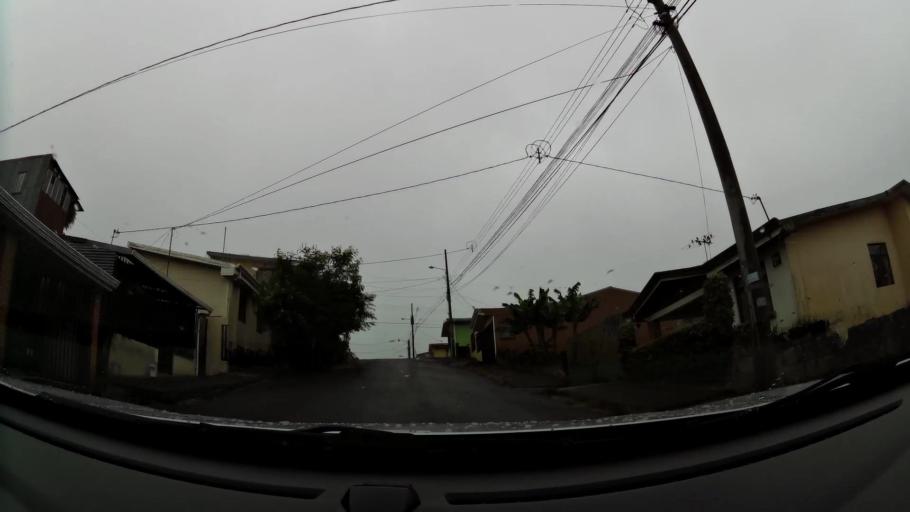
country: CR
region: Cartago
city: Paraiso
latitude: 9.8395
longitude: -83.8615
